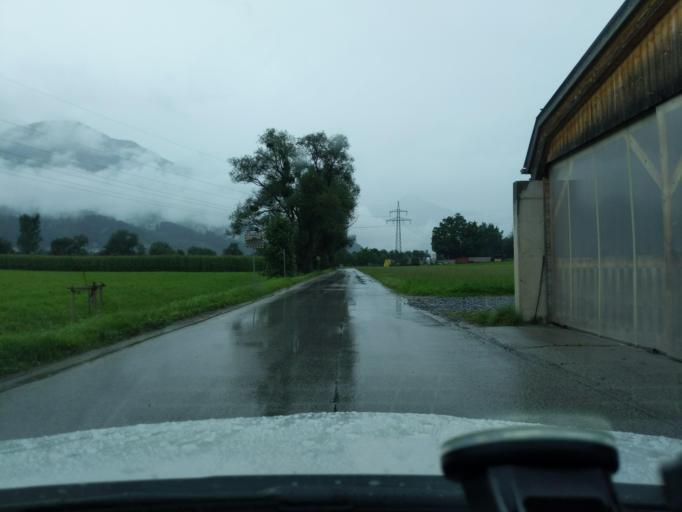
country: AT
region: Tyrol
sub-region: Politischer Bezirk Schwaz
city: Hart im Zillertal
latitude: 47.3424
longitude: 11.8646
